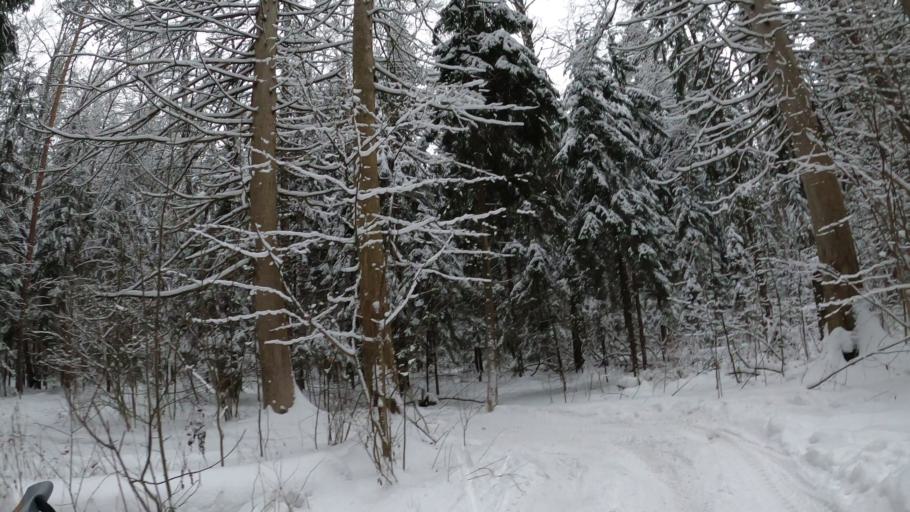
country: RU
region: Moskovskaya
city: Firsanovka
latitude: 55.9316
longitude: 37.2205
